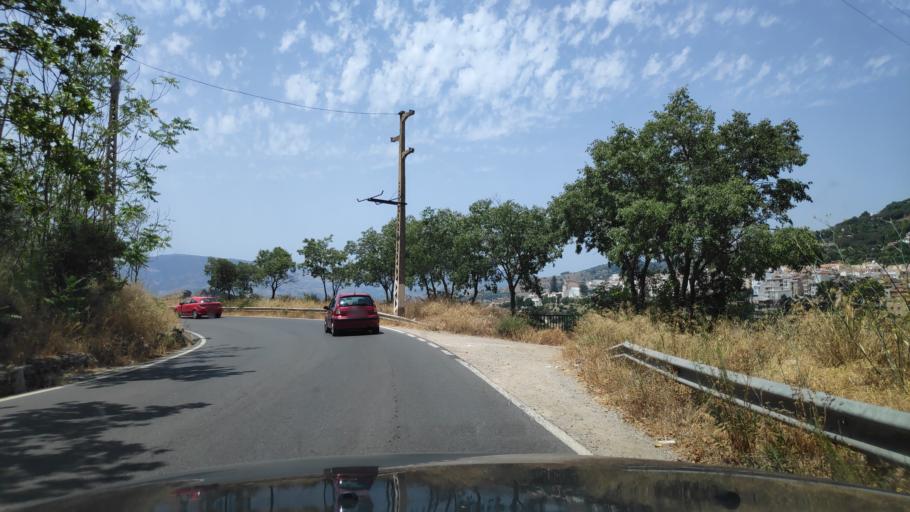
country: ES
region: Andalusia
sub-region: Provincia de Granada
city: Lanjaron
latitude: 36.9174
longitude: -3.4710
